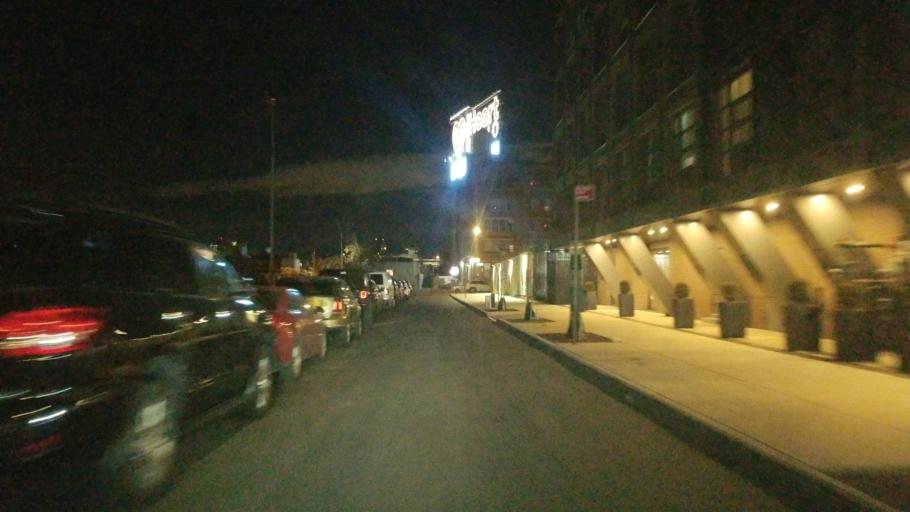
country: US
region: New York
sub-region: New York County
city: Manhattan
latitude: 40.8058
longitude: -73.9270
